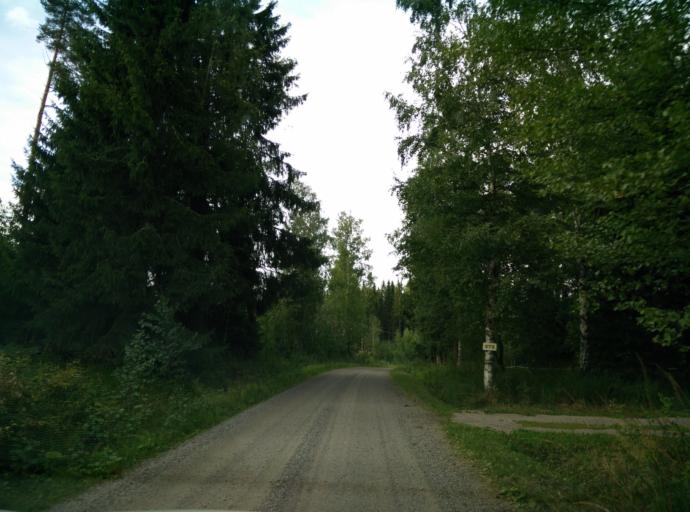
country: FI
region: Haeme
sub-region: Haemeenlinna
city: Kalvola
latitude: 61.1233
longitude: 24.1407
